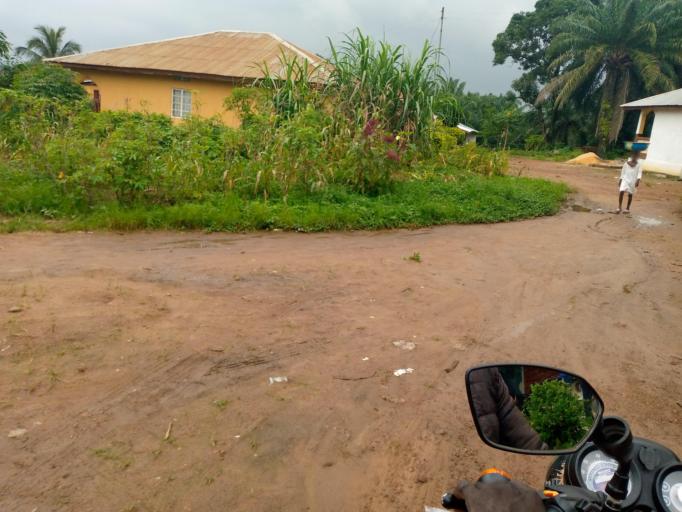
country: SL
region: Eastern Province
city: Kenema
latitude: 7.8823
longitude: -11.1780
